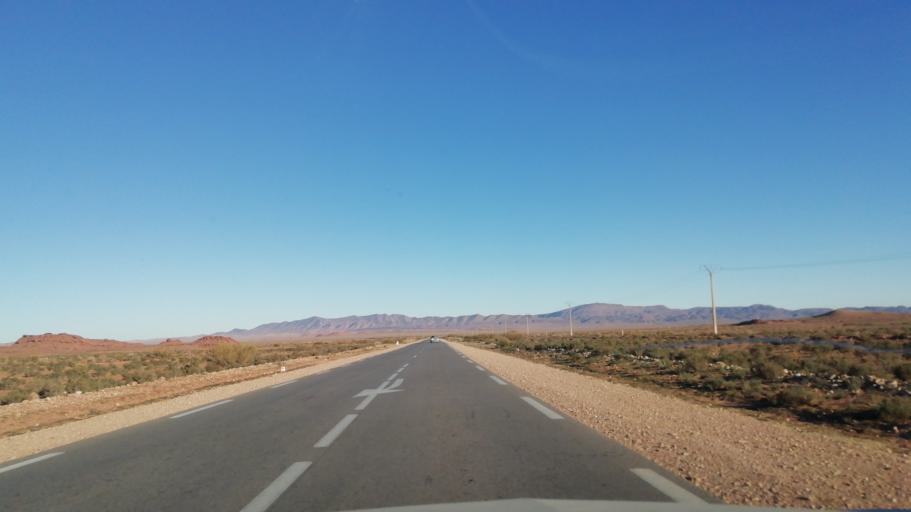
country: DZ
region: El Bayadh
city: El Abiodh Sidi Cheikh
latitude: 33.1704
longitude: 0.4960
